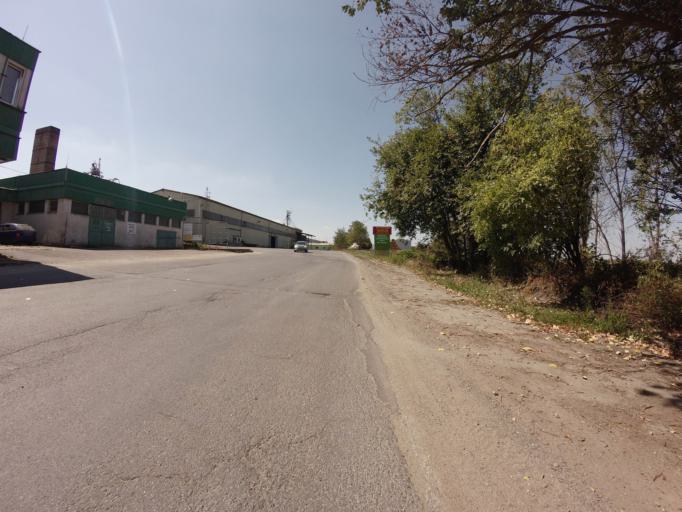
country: CZ
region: Central Bohemia
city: Jilove u Prahy
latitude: 49.9048
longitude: 14.4869
